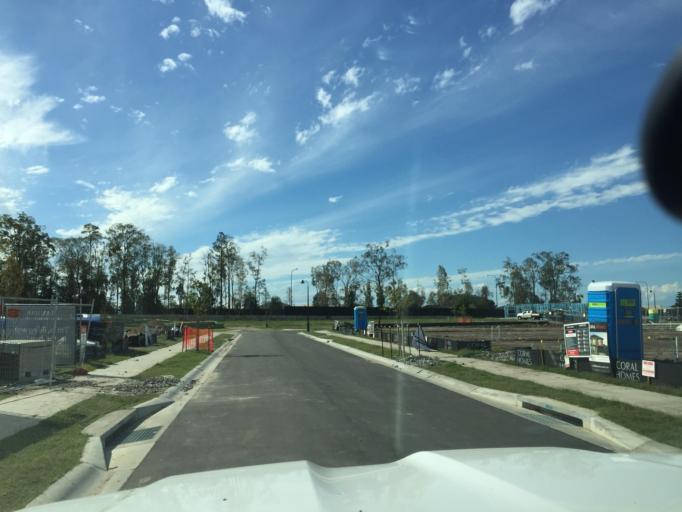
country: AU
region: Queensland
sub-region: Moreton Bay
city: Morayfield
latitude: -27.1249
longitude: 152.9951
